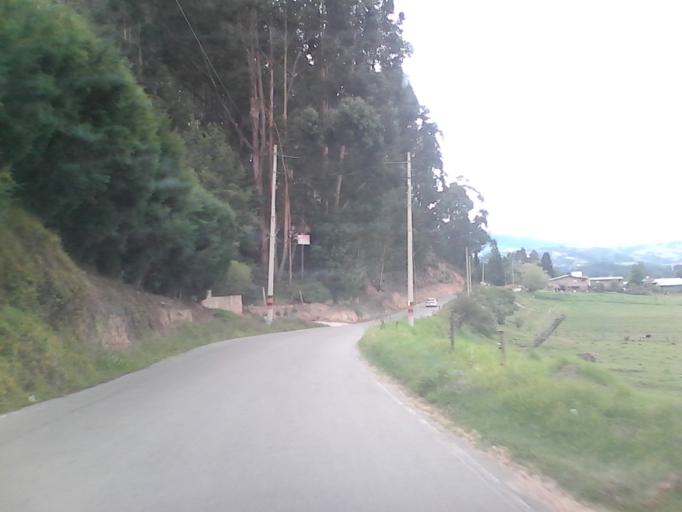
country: CO
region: Boyaca
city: Duitama
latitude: 5.8032
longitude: -73.0625
